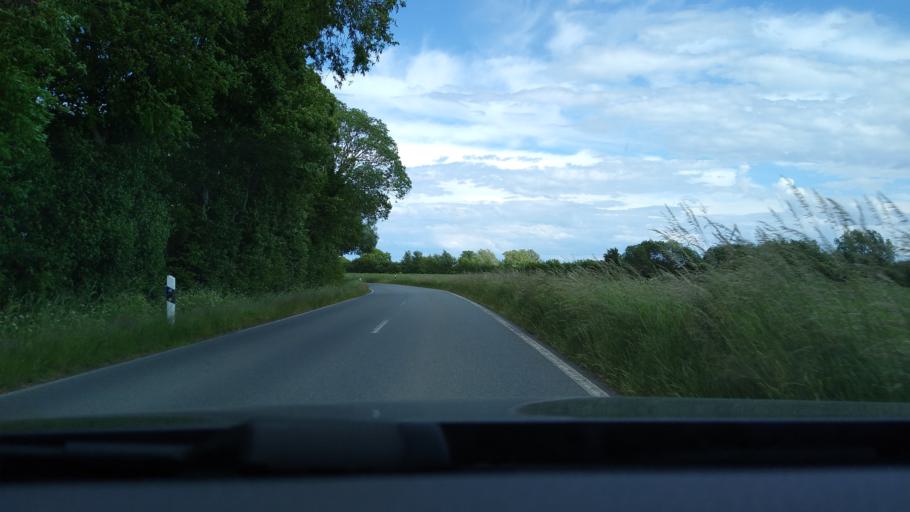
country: DE
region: Schleswig-Holstein
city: Riepsdorf
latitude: 54.2215
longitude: 10.9815
